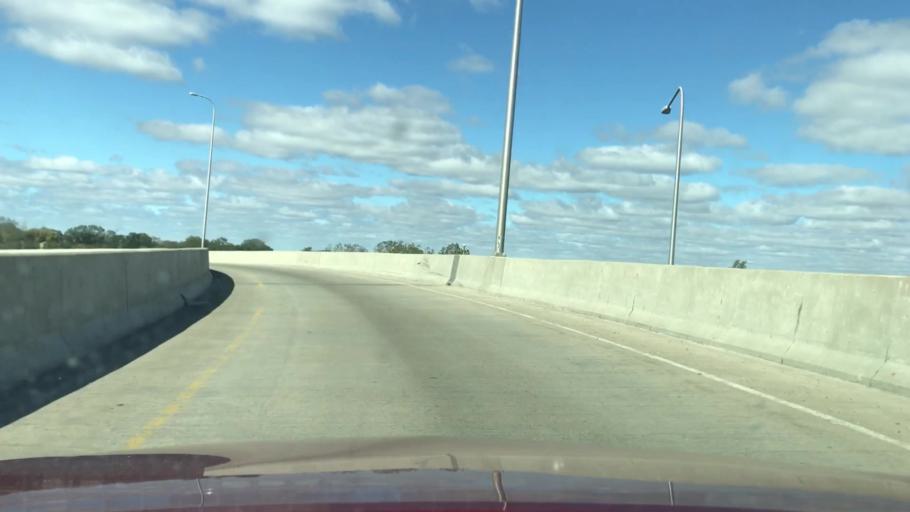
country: US
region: Illinois
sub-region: Cook County
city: Dolton
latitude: 41.7140
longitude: -87.5851
